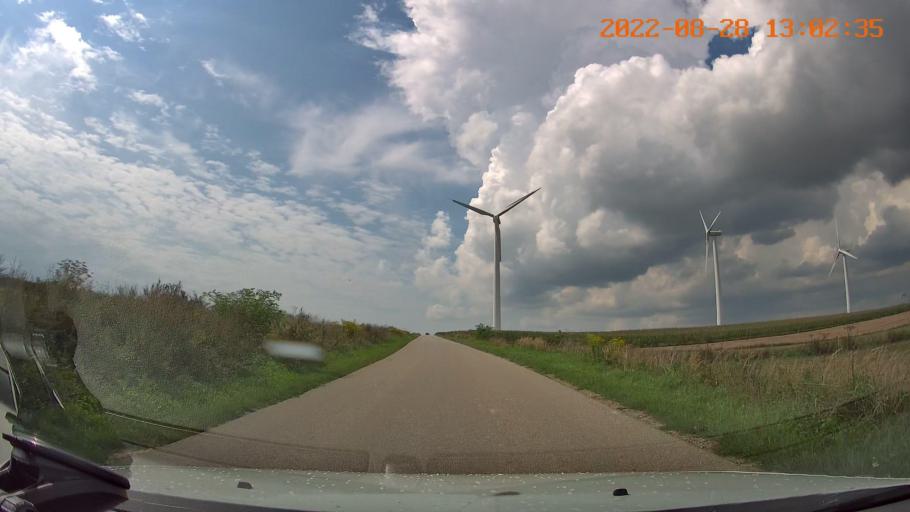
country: PL
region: Lesser Poland Voivodeship
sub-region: Powiat miechowski
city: Miechow
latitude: 50.3562
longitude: 20.1233
